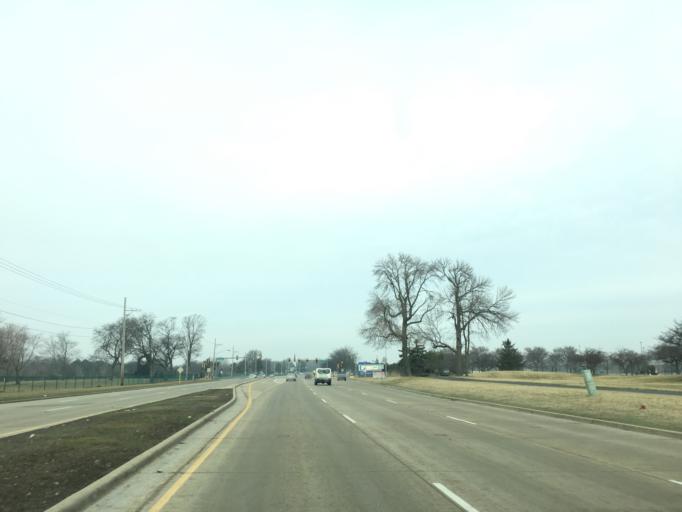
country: US
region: Illinois
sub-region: Cook County
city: Hoffman Estates
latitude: 42.0766
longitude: -88.0707
